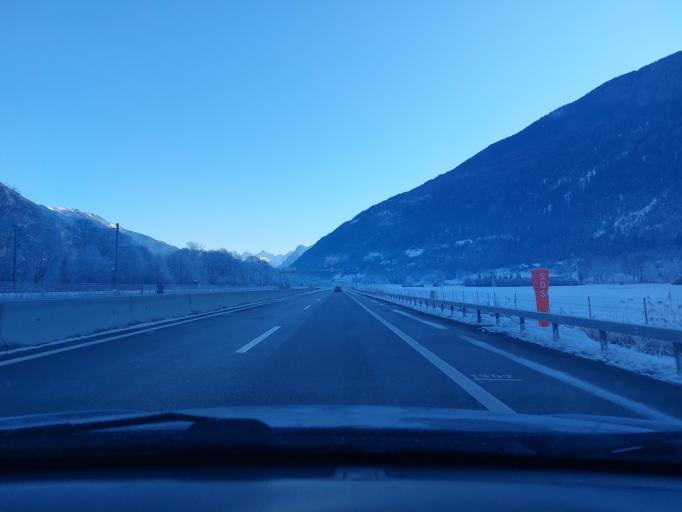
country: CH
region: Valais
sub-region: Leuk District
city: Gampel
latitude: 46.3077
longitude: 7.7240
